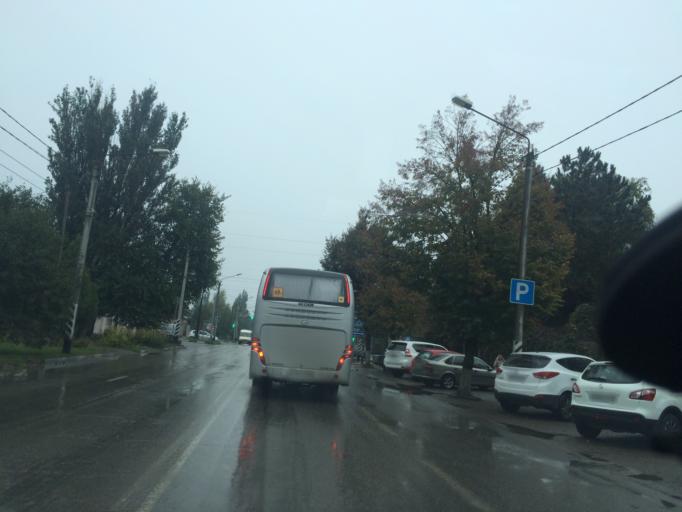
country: RU
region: Rostov
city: Azov
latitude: 47.0952
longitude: 39.4471
